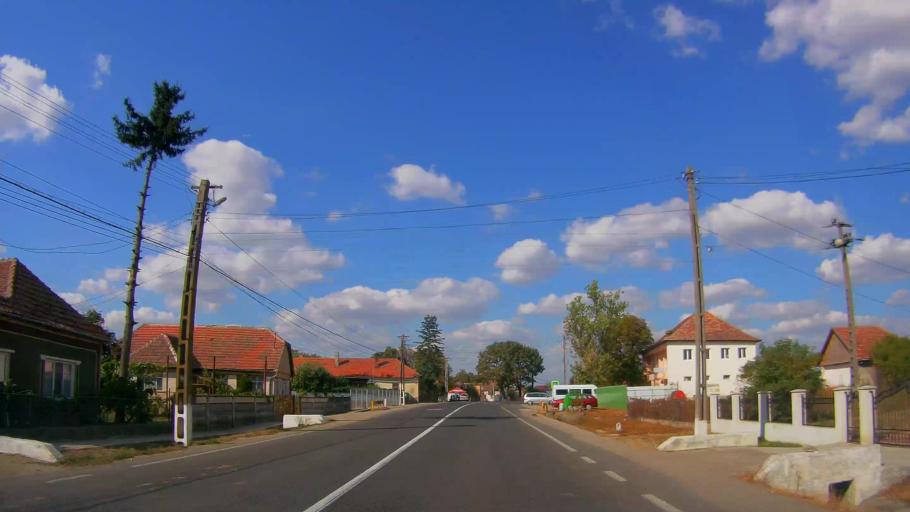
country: RO
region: Satu Mare
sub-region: Comuna Acas
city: Acas
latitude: 47.5375
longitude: 22.7836
